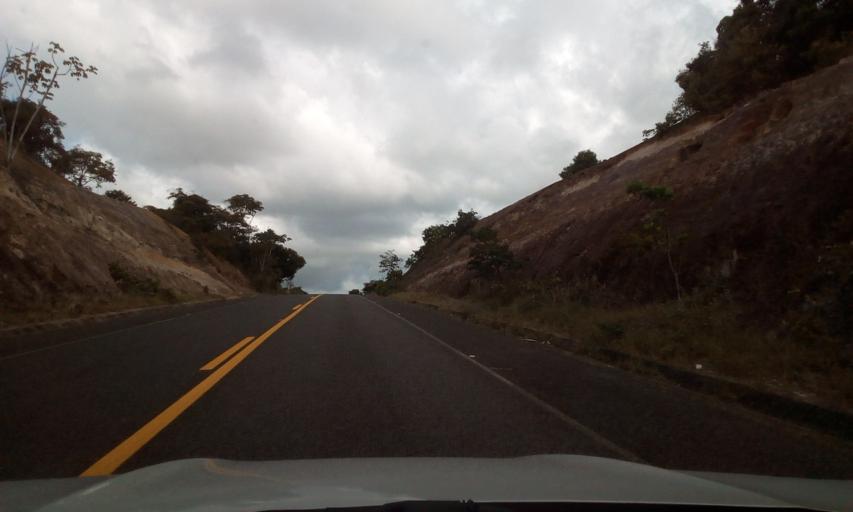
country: BR
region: Sergipe
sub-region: Indiaroba
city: Indiaroba
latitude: -11.5676
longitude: -37.5572
